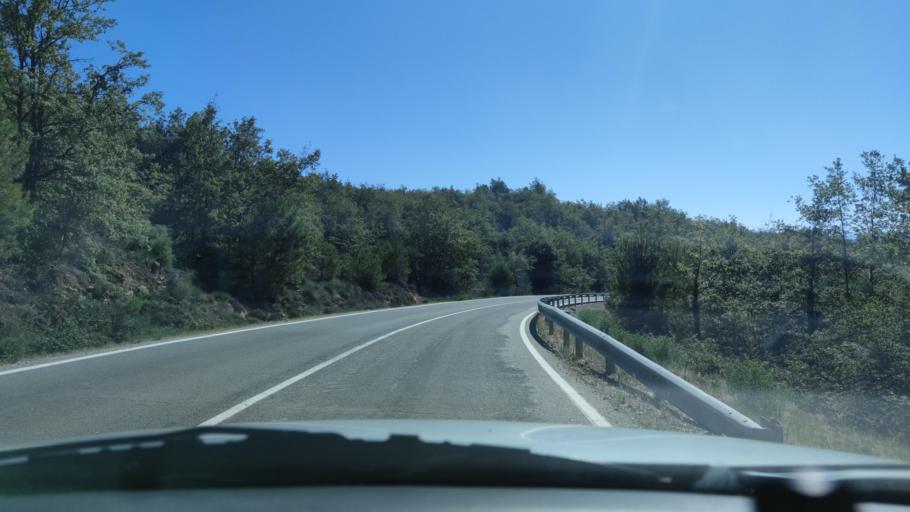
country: ES
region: Catalonia
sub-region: Provincia de Lleida
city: Solsona
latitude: 41.8967
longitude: 1.5588
